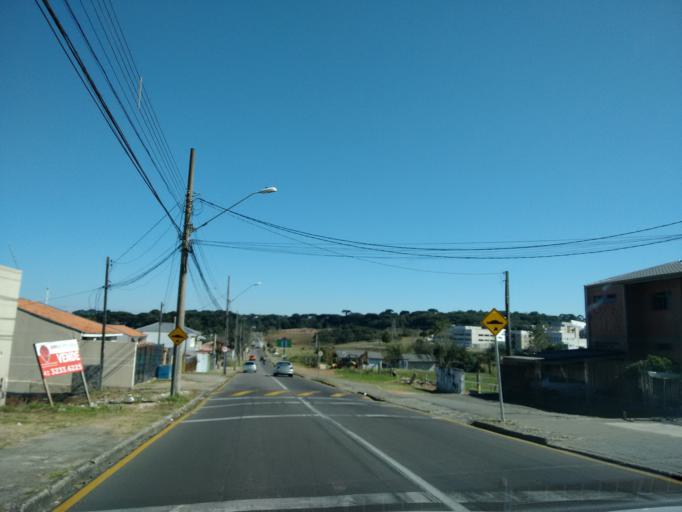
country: BR
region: Parana
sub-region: Curitiba
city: Curitiba
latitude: -25.5121
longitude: -49.3067
